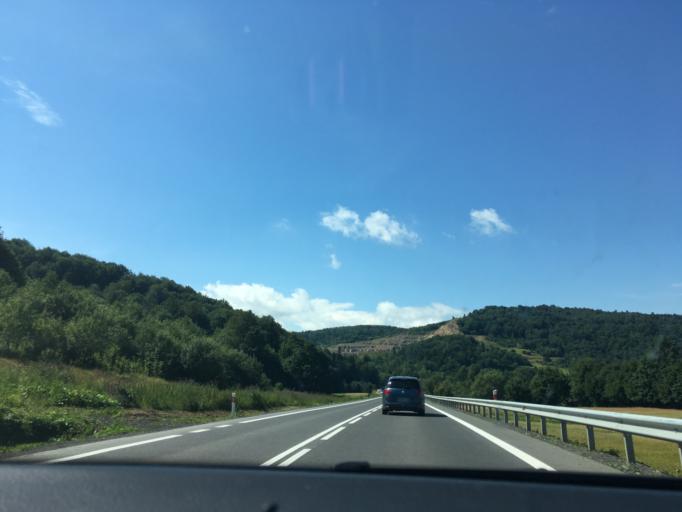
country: PL
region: Subcarpathian Voivodeship
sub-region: Powiat krosnienski
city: Dukla
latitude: 49.5197
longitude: 21.6921
